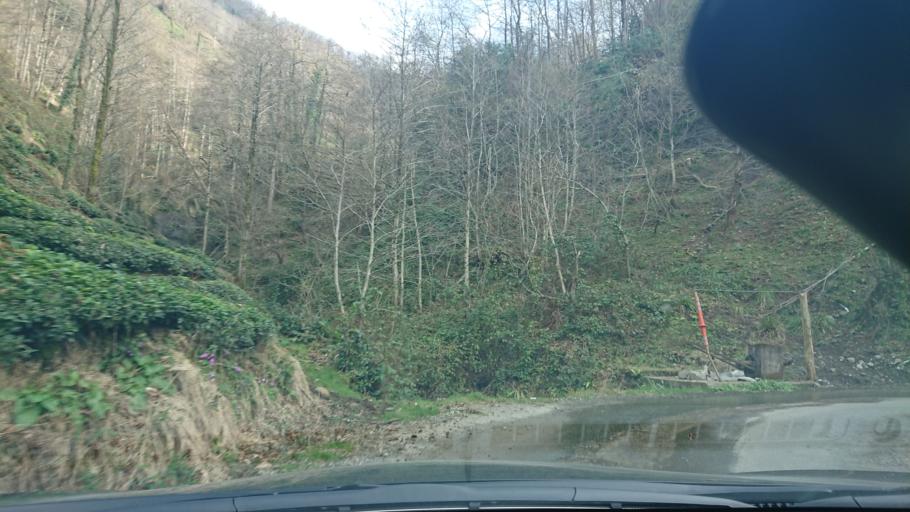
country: TR
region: Rize
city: Rize
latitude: 40.9866
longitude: 40.4953
